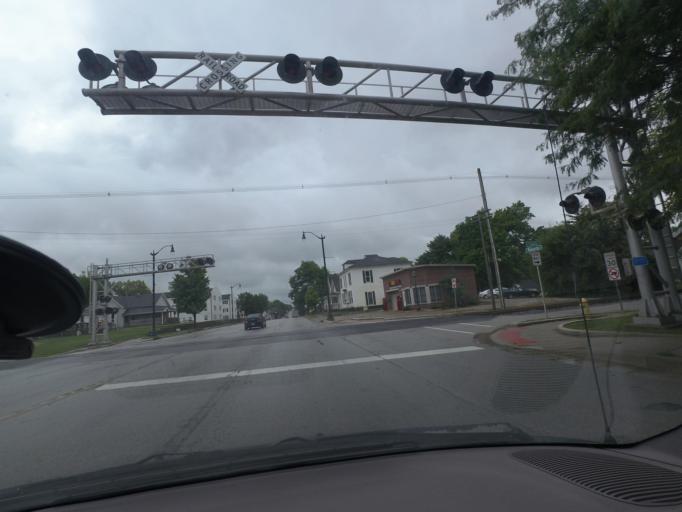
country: US
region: Indiana
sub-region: Montgomery County
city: Crawfordsville
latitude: 40.0363
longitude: -86.9015
